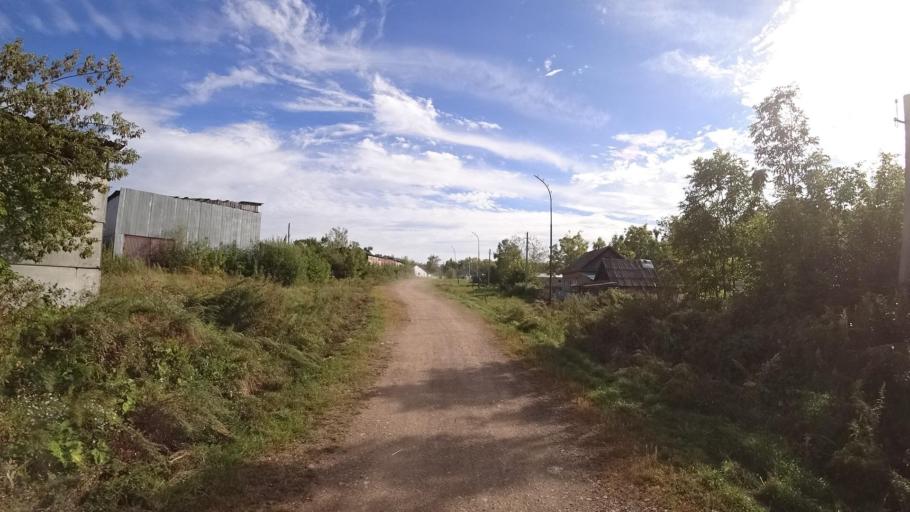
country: RU
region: Primorskiy
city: Dostoyevka
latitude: 44.3022
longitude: 133.4552
